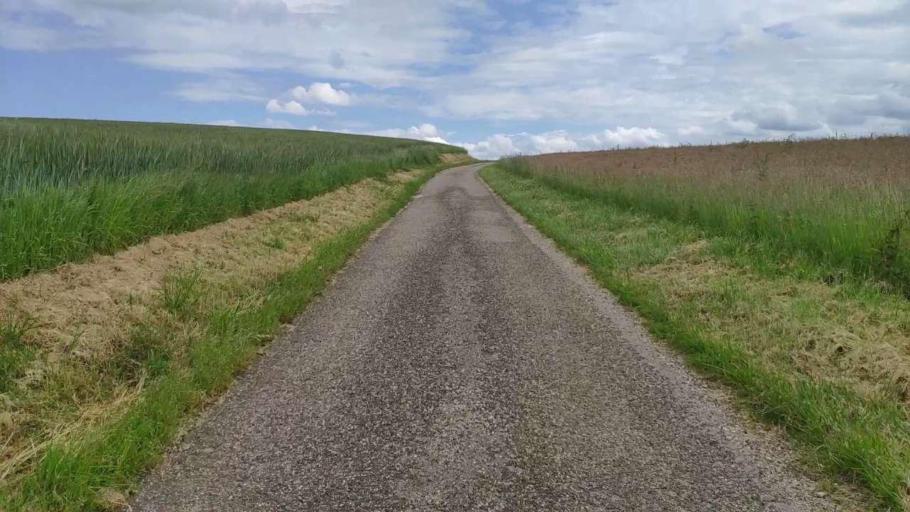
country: FR
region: Franche-Comte
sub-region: Departement du Jura
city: Poligny
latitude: 46.7611
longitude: 5.6462
